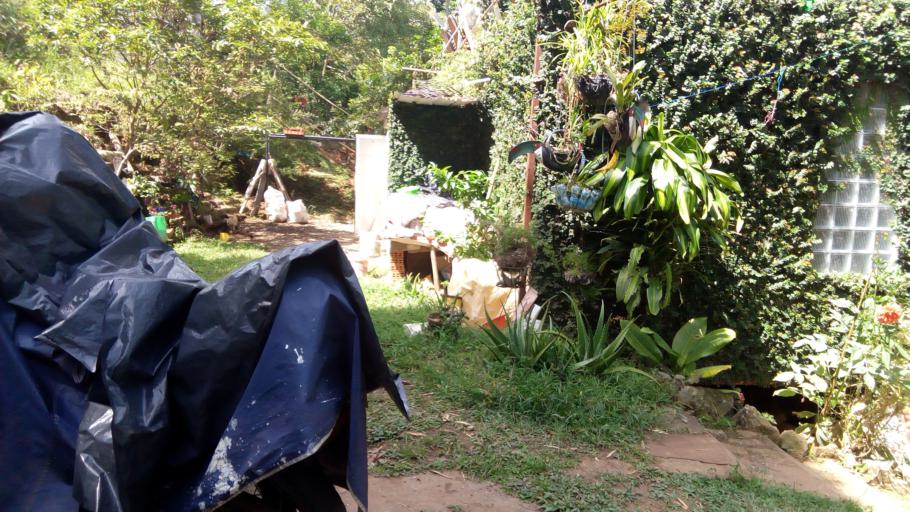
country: CO
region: Valle del Cauca
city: Cali
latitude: 3.4397
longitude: -76.5936
